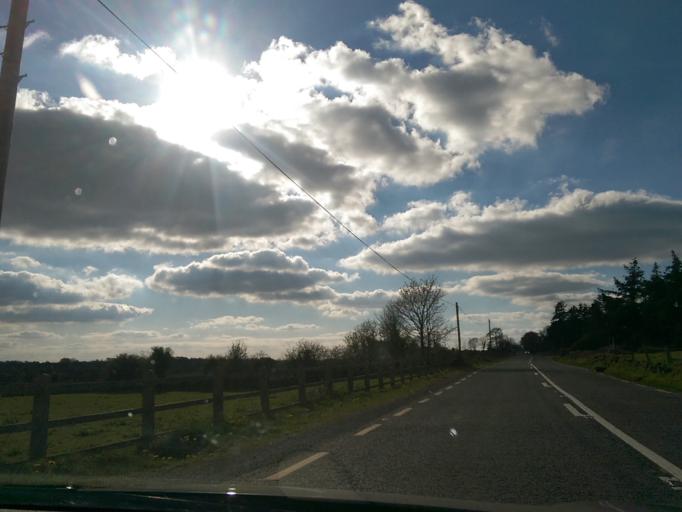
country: IE
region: Connaught
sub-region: County Galway
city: Portumna
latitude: 53.1883
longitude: -8.3669
